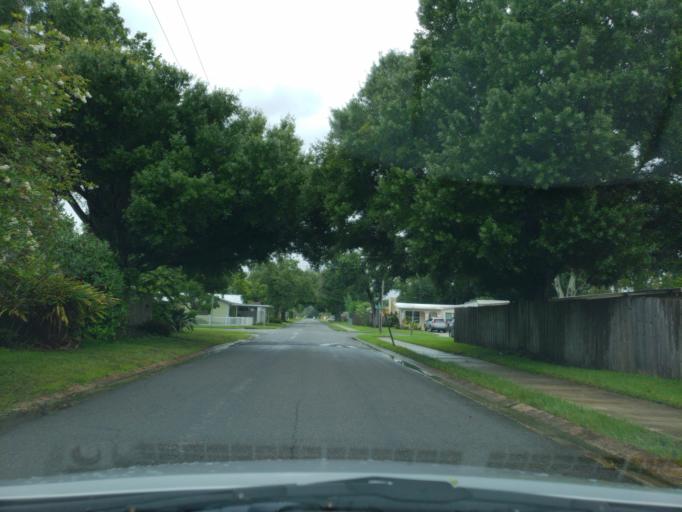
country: US
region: Florida
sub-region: Hillsborough County
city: Egypt Lake-Leto
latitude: 28.0053
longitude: -82.5104
